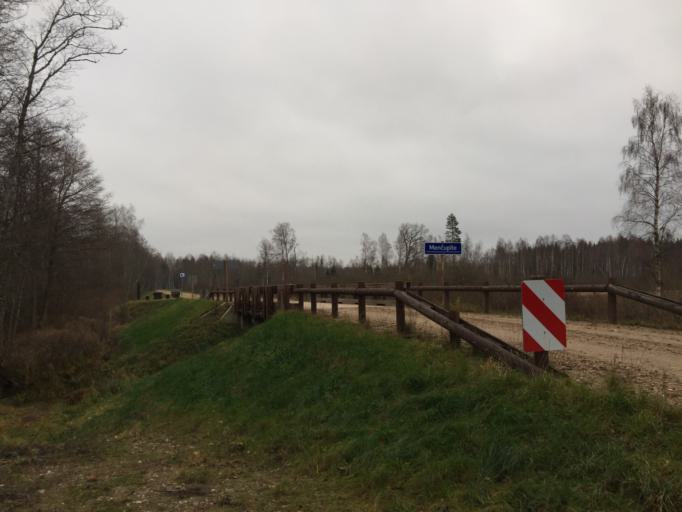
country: LV
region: Burtnieki
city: Matisi
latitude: 57.5469
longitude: 25.1481
